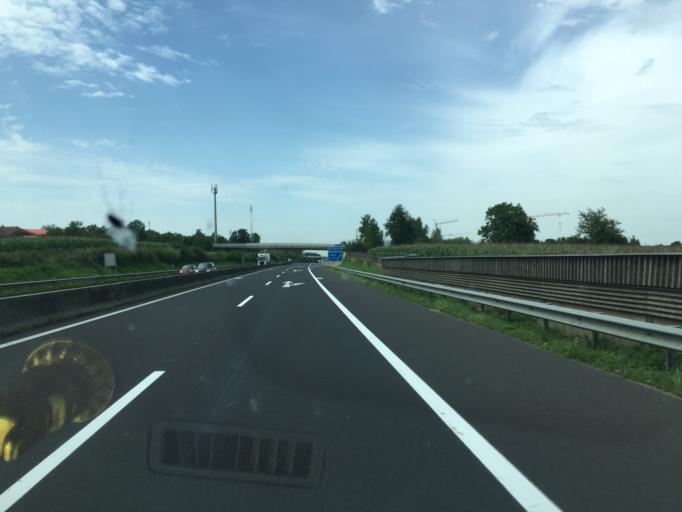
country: AT
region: Upper Austria
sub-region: Wels-Land
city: Sattledt
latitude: 48.0127
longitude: 14.0699
